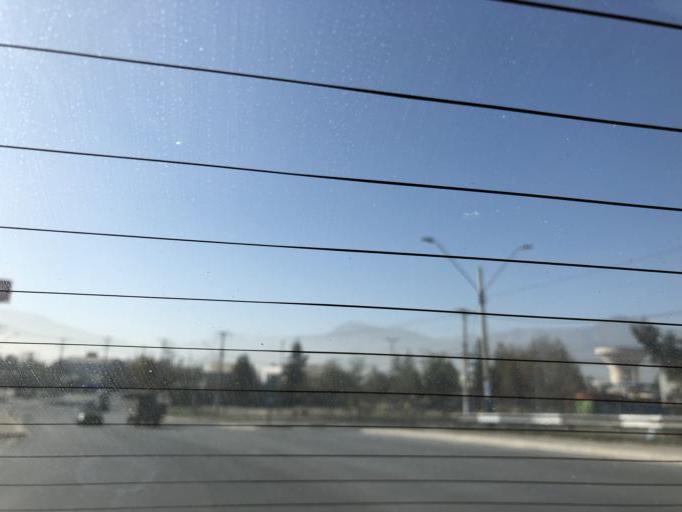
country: CL
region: Santiago Metropolitan
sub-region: Provincia de Cordillera
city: Puente Alto
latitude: -33.6154
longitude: -70.5991
